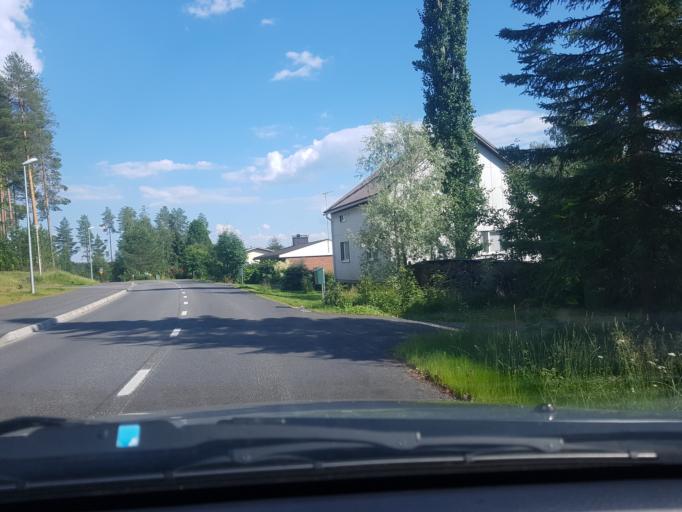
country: FI
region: Kainuu
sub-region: Kehys-Kainuu
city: Kuhmo
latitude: 64.1276
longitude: 29.5384
